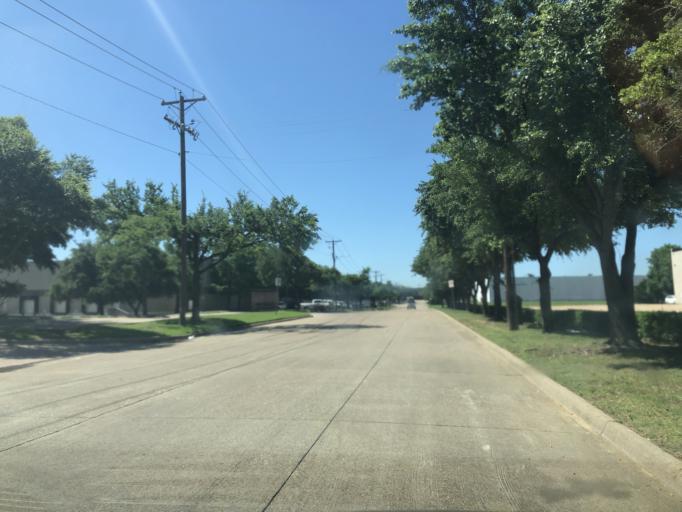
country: US
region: Texas
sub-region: Tarrant County
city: Euless
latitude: 32.7983
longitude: -97.0446
